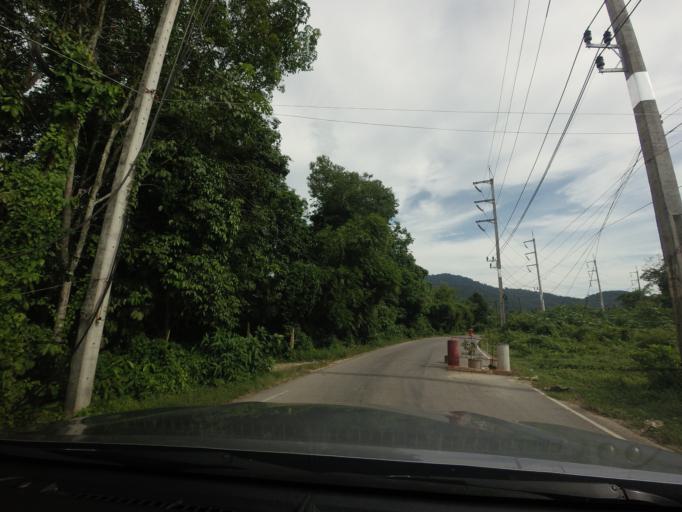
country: TH
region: Yala
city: Yala
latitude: 6.5065
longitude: 101.2890
